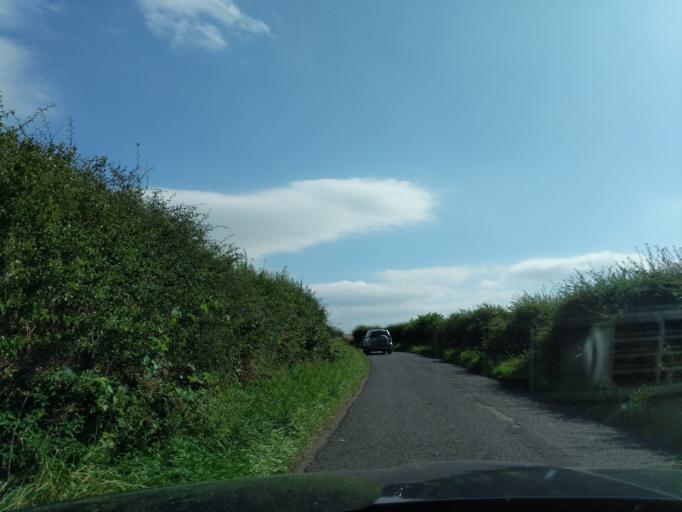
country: GB
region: England
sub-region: Northumberland
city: Ford
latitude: 55.6670
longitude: -2.1646
